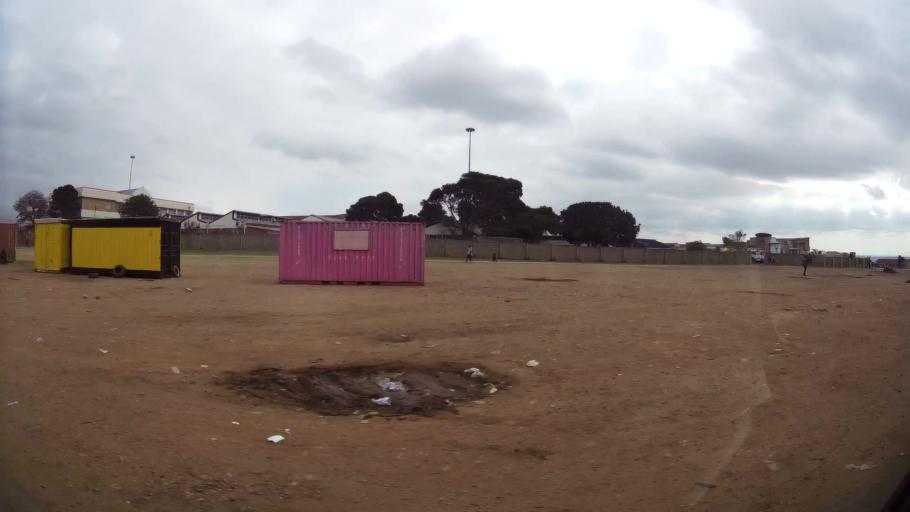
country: ZA
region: Eastern Cape
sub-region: Nelson Mandela Bay Metropolitan Municipality
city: Port Elizabeth
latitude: -33.8816
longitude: 25.5637
